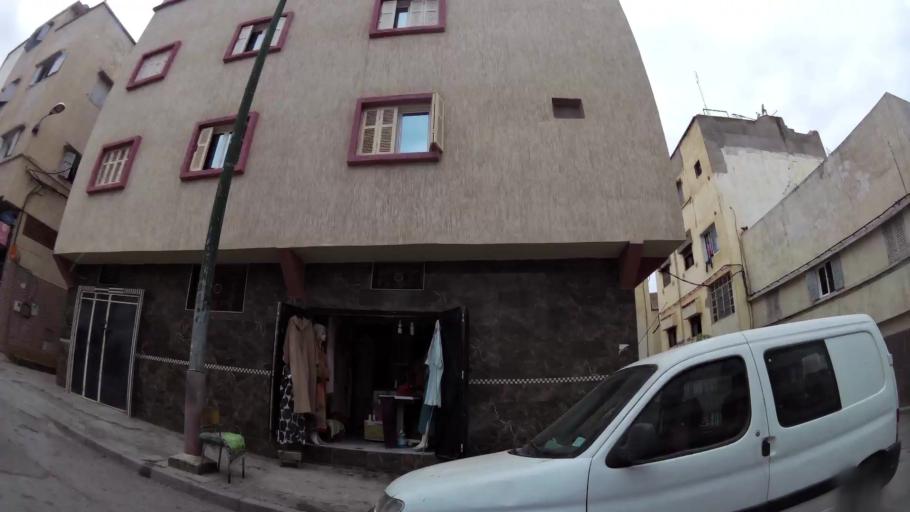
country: MA
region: Rabat-Sale-Zemmour-Zaer
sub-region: Rabat
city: Rabat
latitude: 34.0025
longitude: -6.8676
